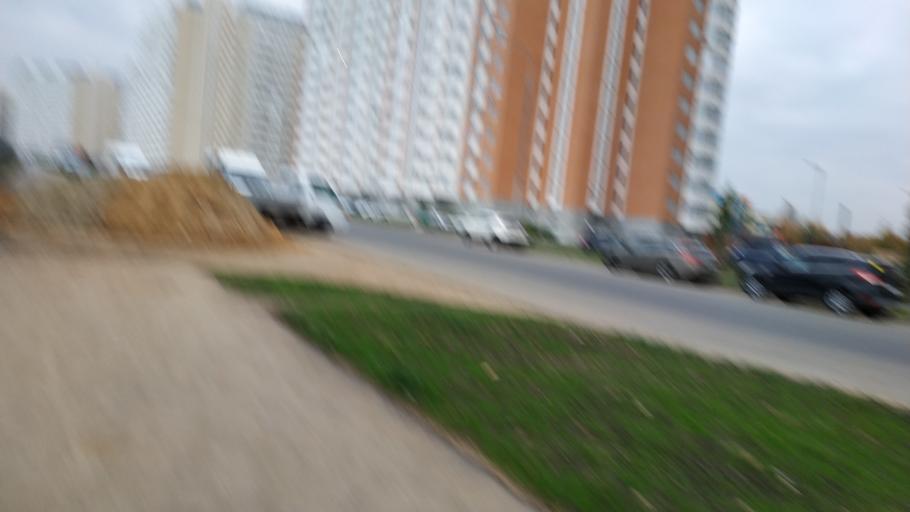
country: RU
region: Moscow
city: Novo-Peredelkino
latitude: 55.6372
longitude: 37.3159
